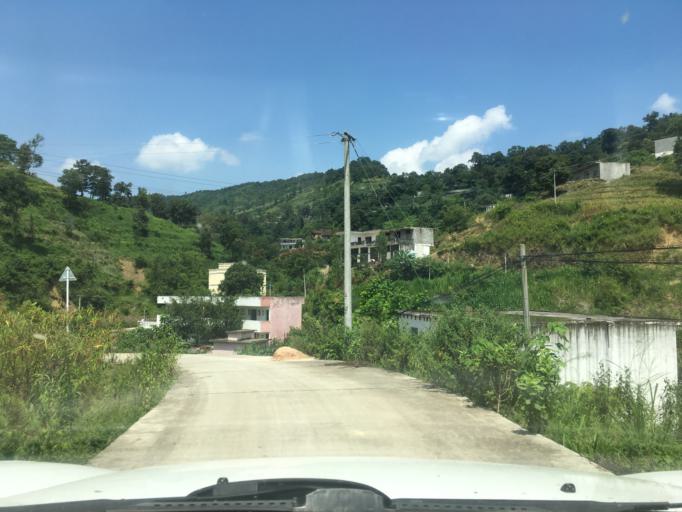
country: CN
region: Guangxi Zhuangzu Zizhiqu
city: Xinzhou
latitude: 25.4601
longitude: 105.7716
